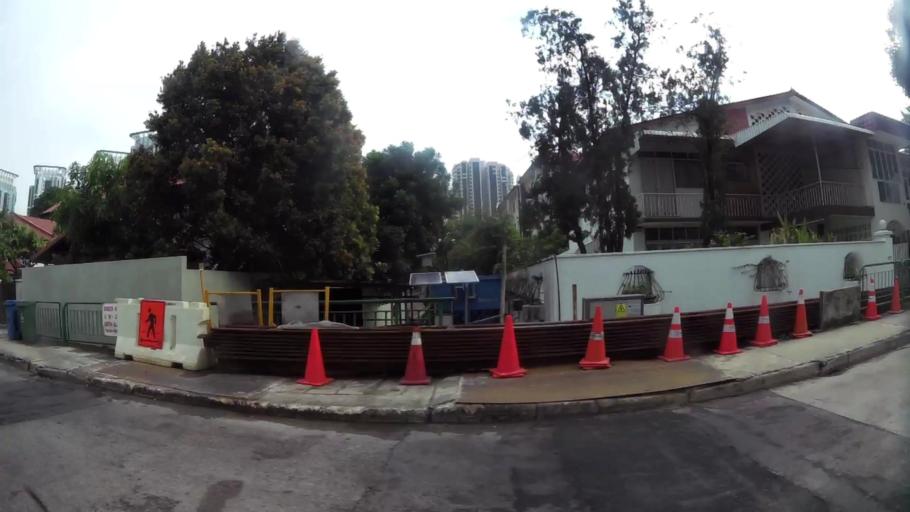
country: SG
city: Singapore
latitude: 1.3144
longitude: 103.9360
